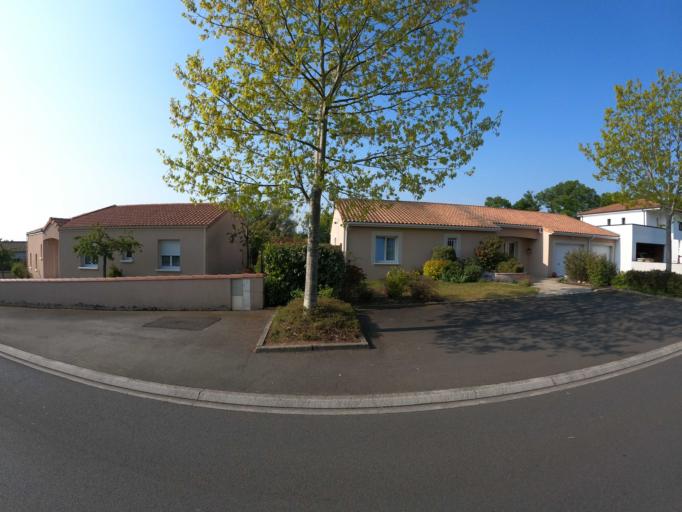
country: FR
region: Pays de la Loire
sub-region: Departement de Maine-et-Loire
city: La Seguiniere
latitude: 47.0662
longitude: -0.9466
